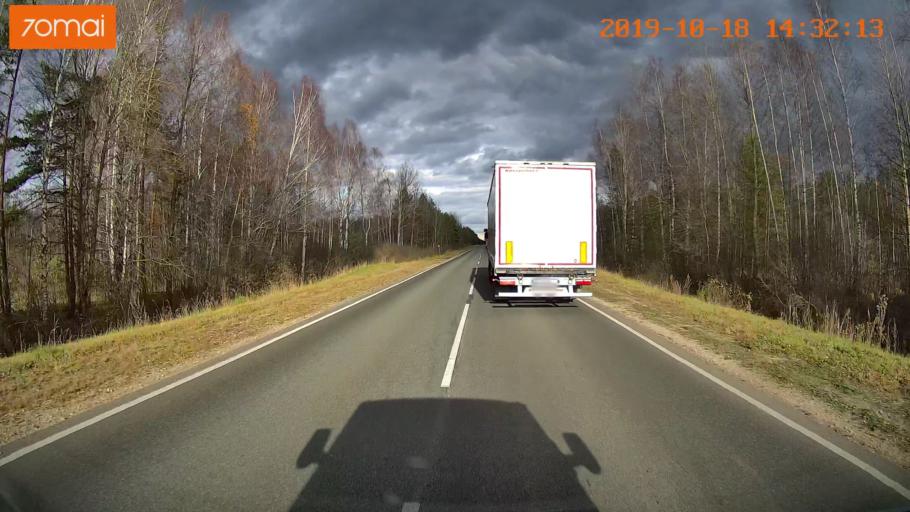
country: RU
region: Rjazan
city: Tuma
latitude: 55.1892
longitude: 40.5762
